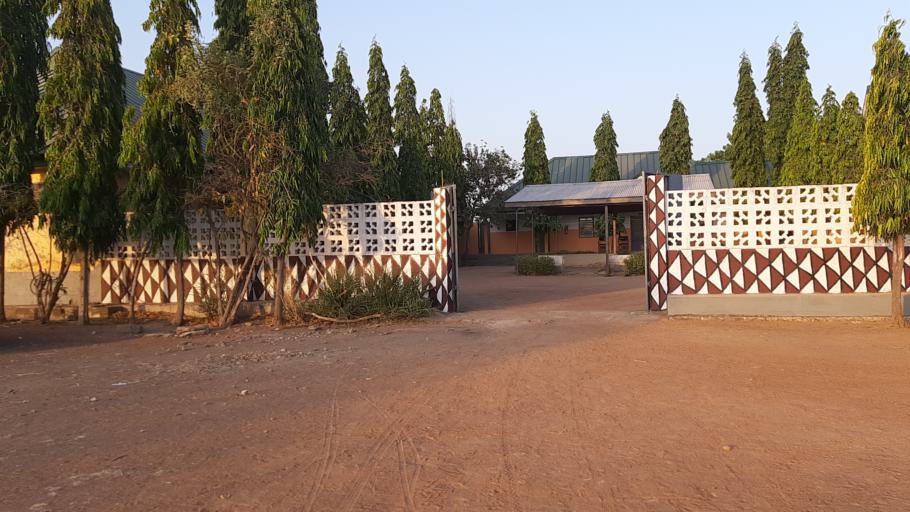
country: GH
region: Upper East
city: Bolgatanga
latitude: 10.6720
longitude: -0.8648
